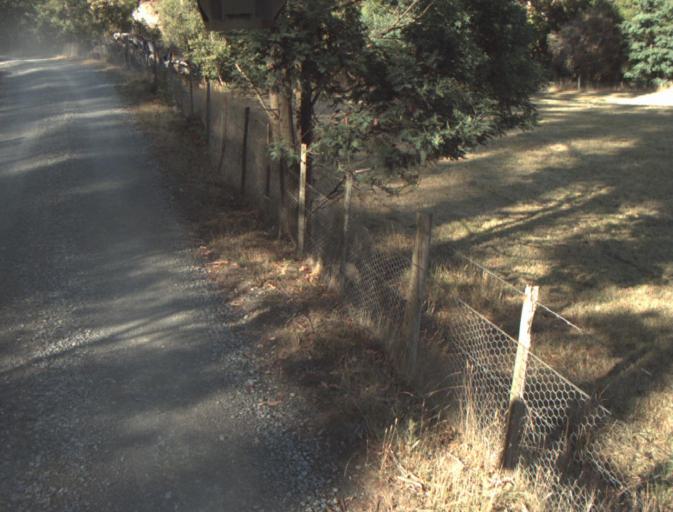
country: AU
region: Tasmania
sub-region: Launceston
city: Mayfield
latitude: -41.2884
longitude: 147.1973
